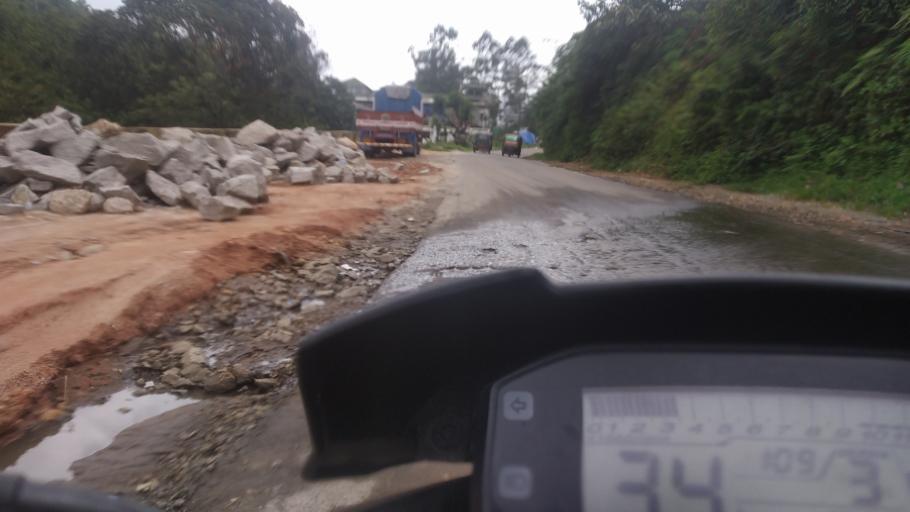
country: IN
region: Kerala
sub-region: Idukki
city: Munnar
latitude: 10.0844
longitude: 77.0636
